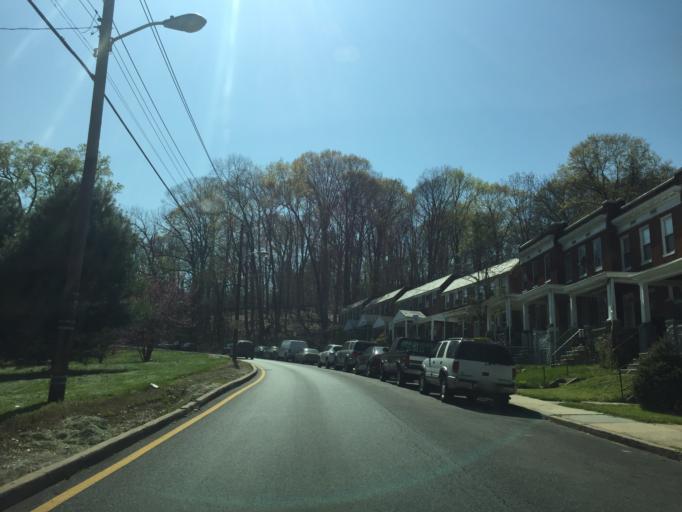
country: US
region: Maryland
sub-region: City of Baltimore
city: Baltimore
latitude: 39.3303
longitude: -76.6543
